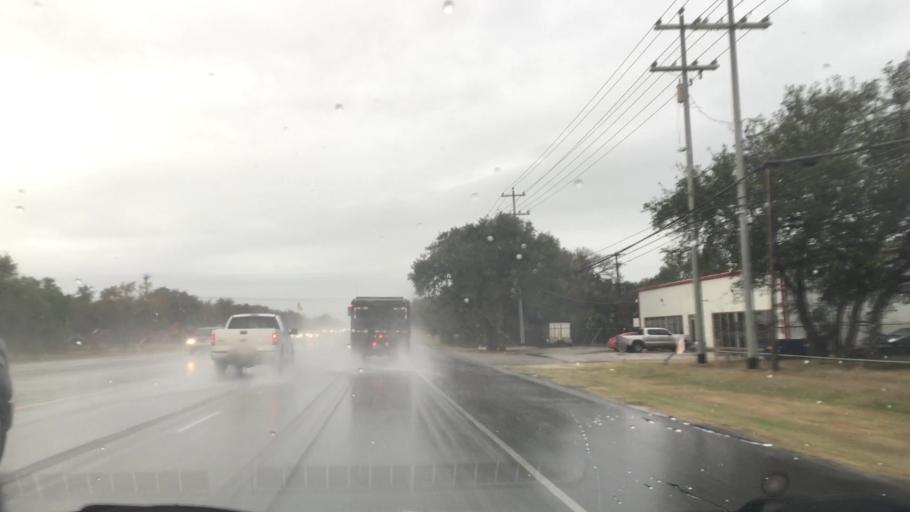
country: US
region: Texas
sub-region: Williamson County
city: Anderson Mill
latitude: 30.4412
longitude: -97.8347
